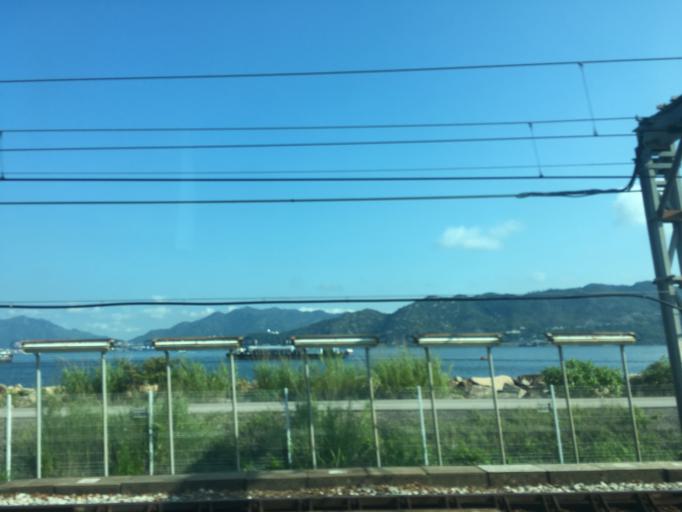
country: HK
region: Tsuen Wan
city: Tsuen Wan
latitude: 22.3379
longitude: 114.0372
